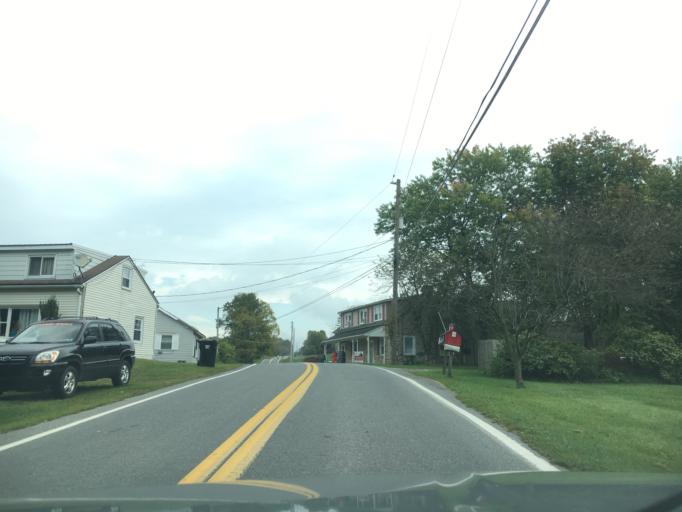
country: US
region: Pennsylvania
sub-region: Berks County
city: Fleetwood
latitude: 40.4539
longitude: -75.7581
